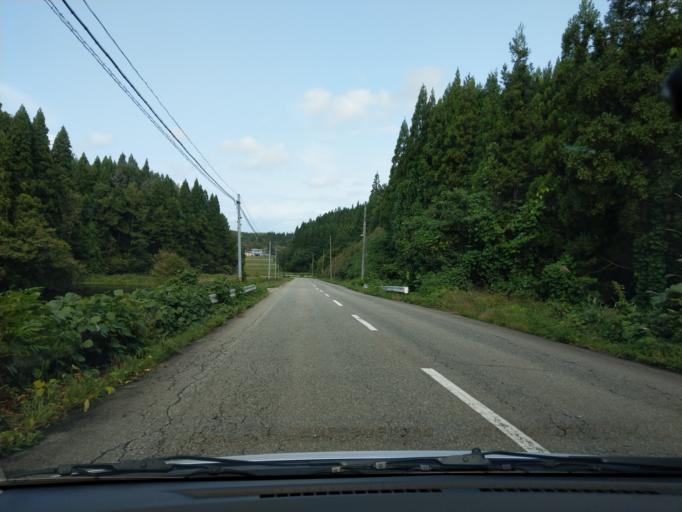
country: JP
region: Akita
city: Omagari
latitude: 39.5141
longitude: 140.3068
